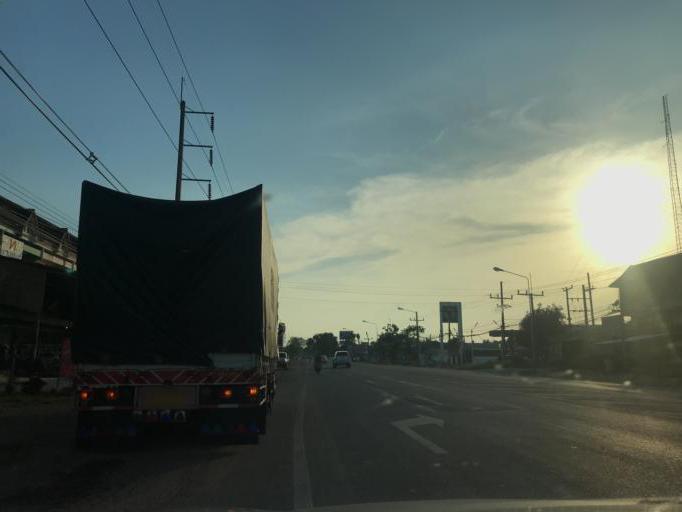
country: TH
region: Phayao
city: Chiang Kham
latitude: 19.5169
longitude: 100.2933
